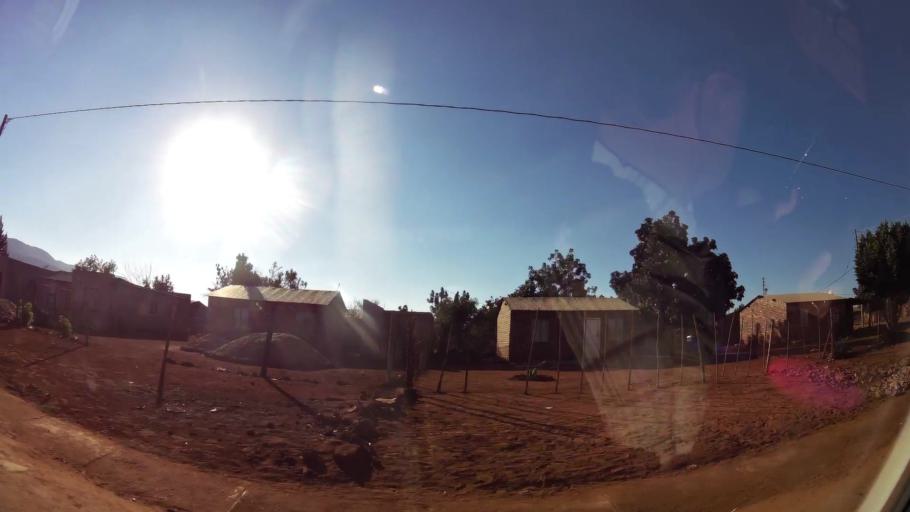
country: ZA
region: Limpopo
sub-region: Waterberg District Municipality
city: Mokopane
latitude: -24.1821
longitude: 28.9771
